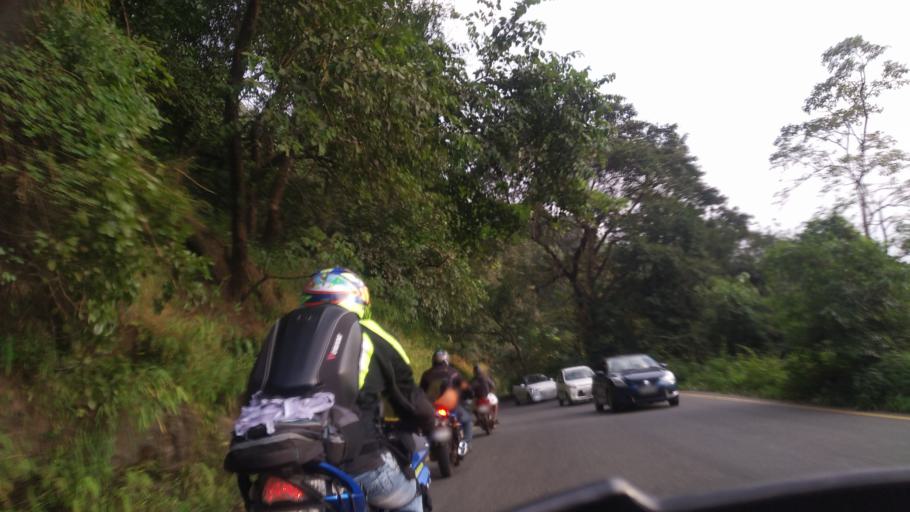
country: IN
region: Kerala
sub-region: Wayanad
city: Kalpetta
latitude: 11.5157
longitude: 76.0144
